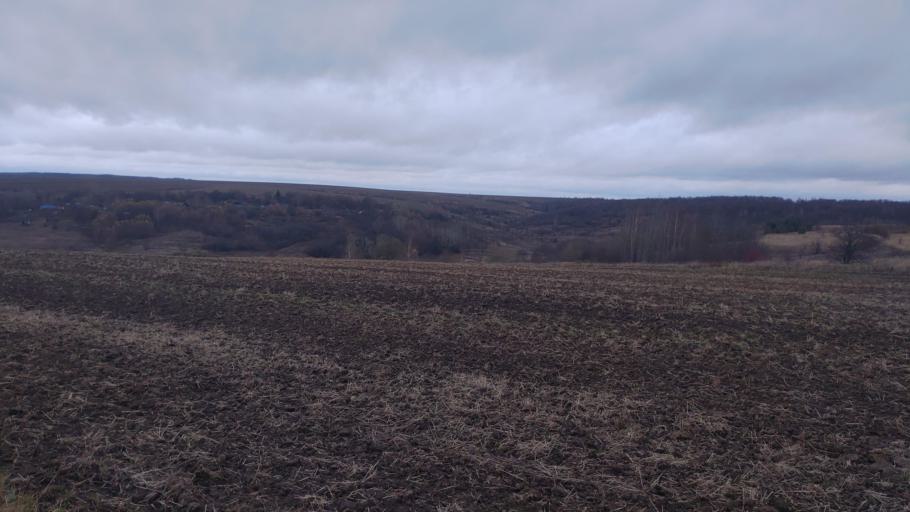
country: RU
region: Nizjnij Novgorod
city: Vad
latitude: 55.6088
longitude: 44.3254
